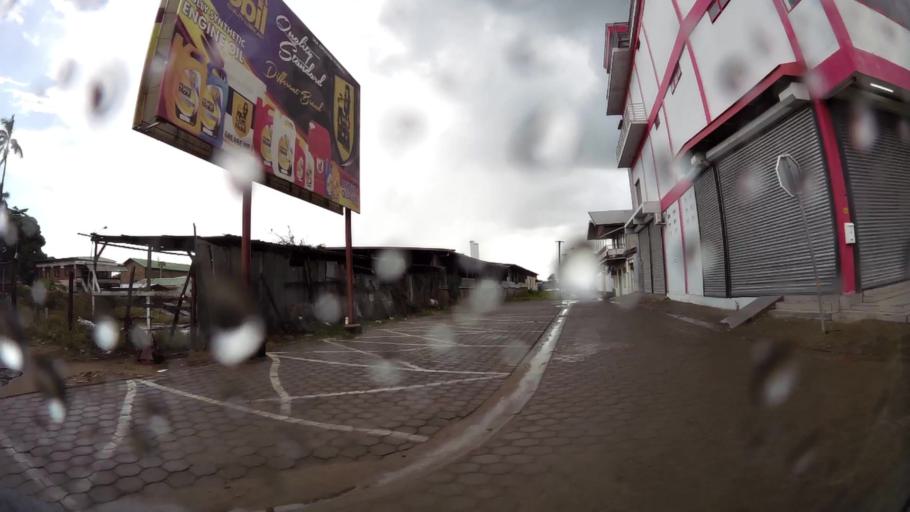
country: SR
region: Paramaribo
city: Paramaribo
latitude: 5.8214
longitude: -55.1649
